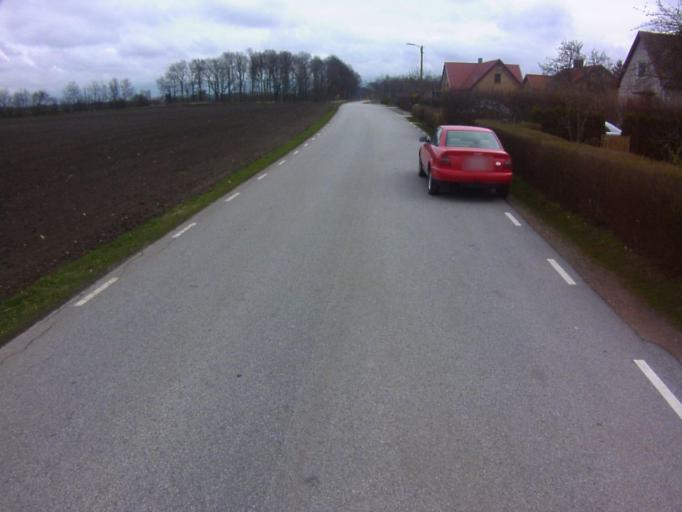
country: SE
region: Skane
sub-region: Lunds Kommun
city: Lund
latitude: 55.7916
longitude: 13.2138
